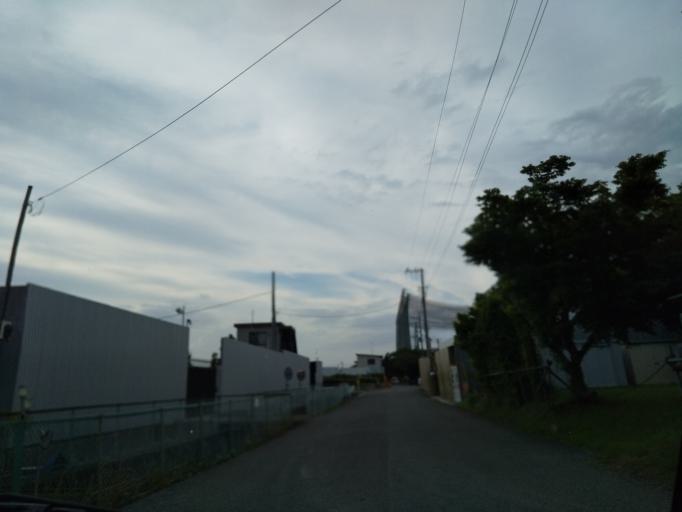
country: JP
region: Kanagawa
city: Zama
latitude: 35.4715
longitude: 139.3614
